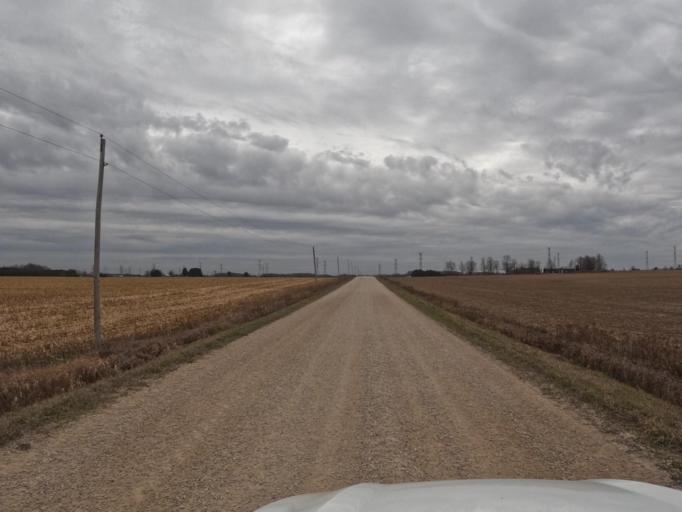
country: CA
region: Ontario
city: Shelburne
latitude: 43.9986
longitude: -80.3866
